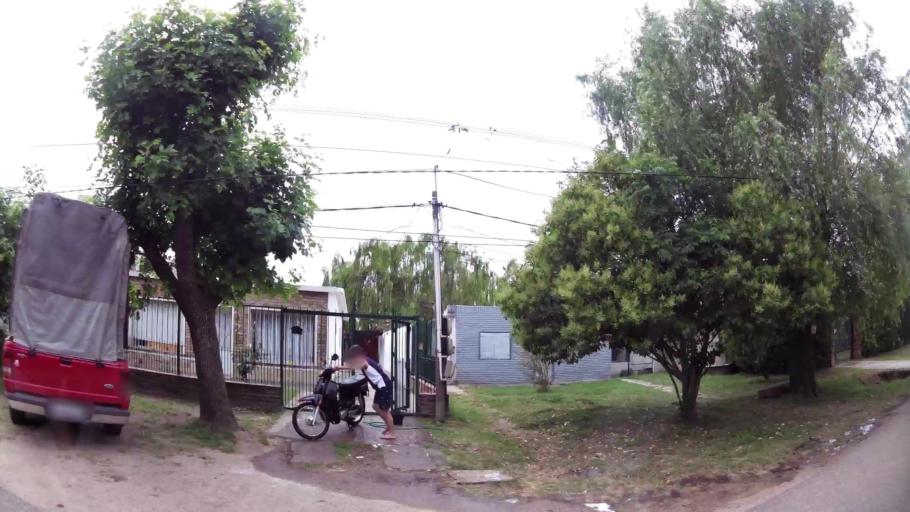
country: UY
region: Canelones
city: La Paz
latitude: -34.7570
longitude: -56.2258
